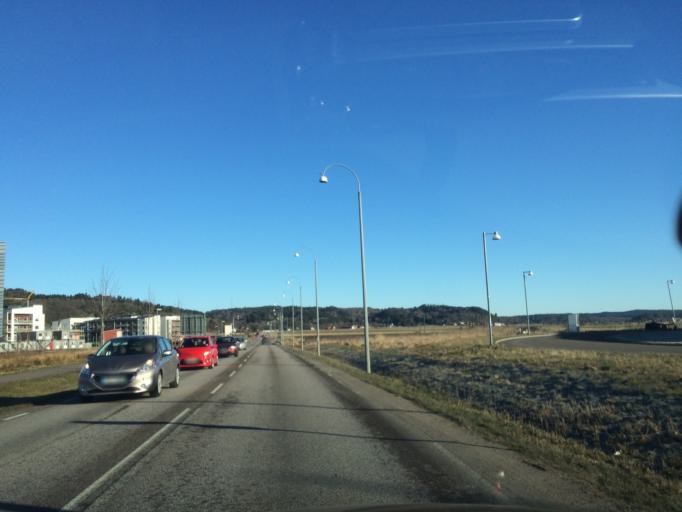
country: SE
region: Halland
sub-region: Kungsbacka Kommun
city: Kungsbacka
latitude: 57.5147
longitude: 12.0811
